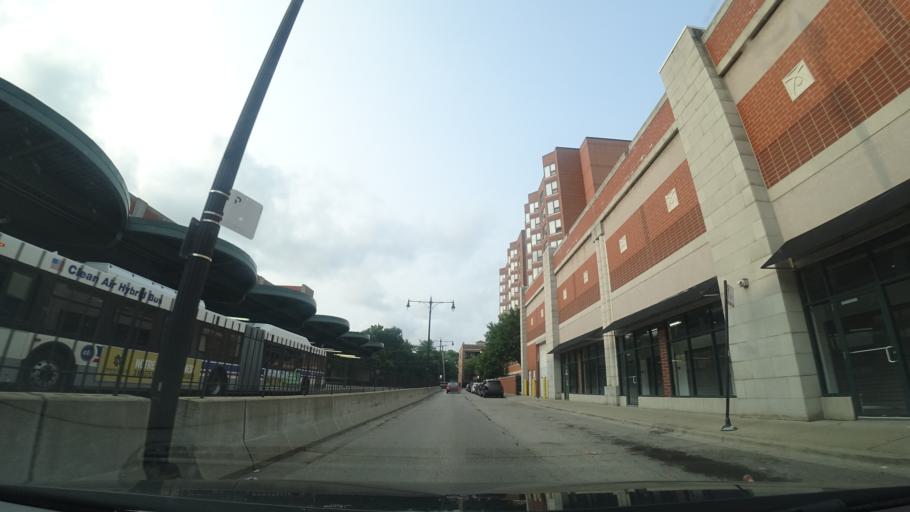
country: US
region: Illinois
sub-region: Cook County
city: Evanston
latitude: 42.0179
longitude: -87.6732
